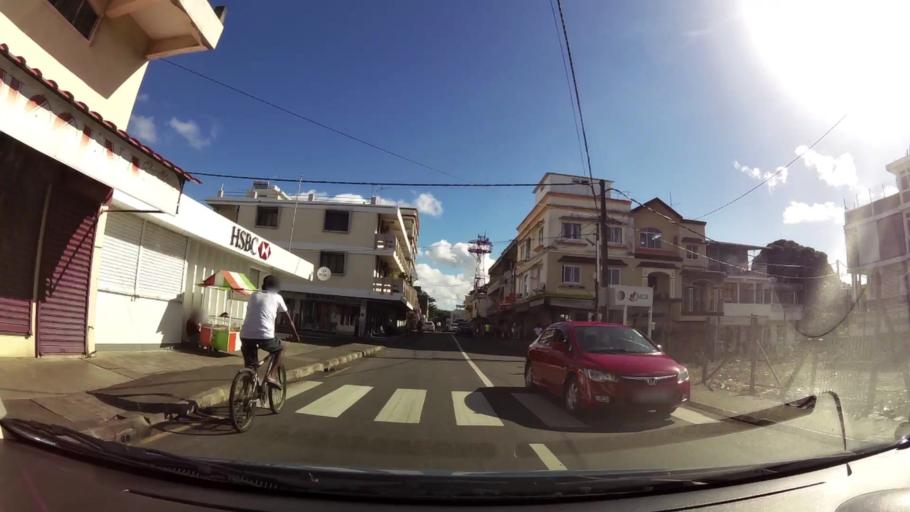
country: MU
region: Grand Port
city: Mahebourg
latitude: -20.4090
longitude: 57.7064
